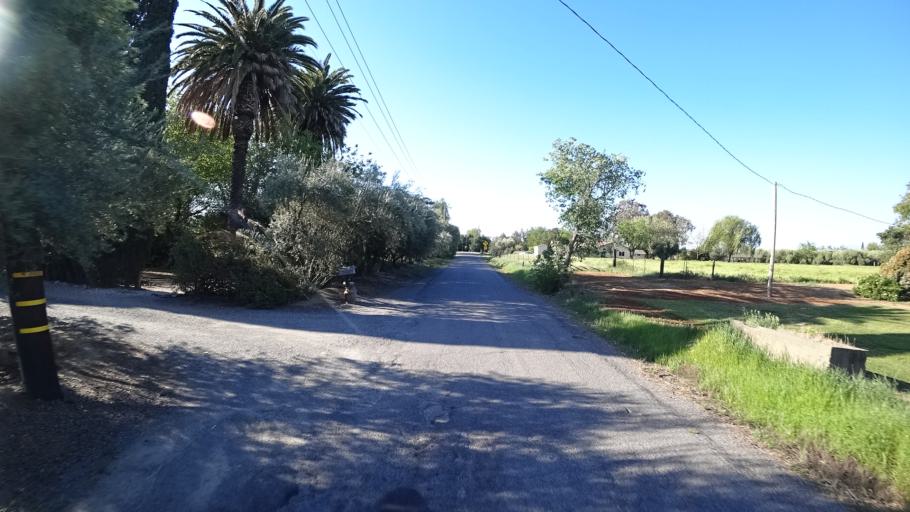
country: US
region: California
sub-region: Glenn County
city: Orland
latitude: 39.7234
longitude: -122.1878
